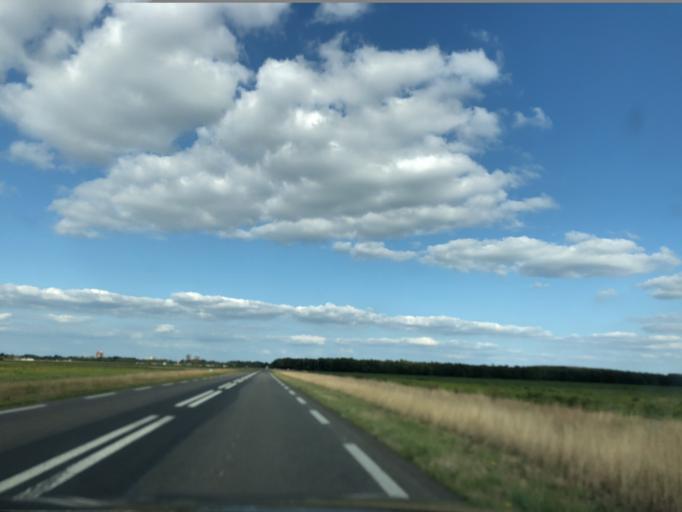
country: NL
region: Groningen
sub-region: Gemeente Stadskanaal
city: Stadskanaal
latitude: 52.9740
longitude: 6.9266
